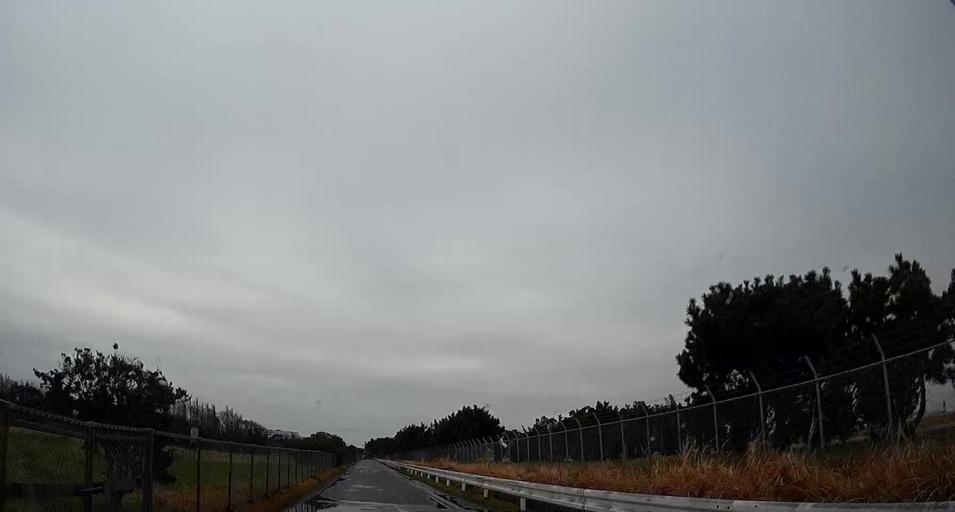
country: JP
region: Chiba
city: Kisarazu
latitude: 35.4071
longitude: 139.9131
